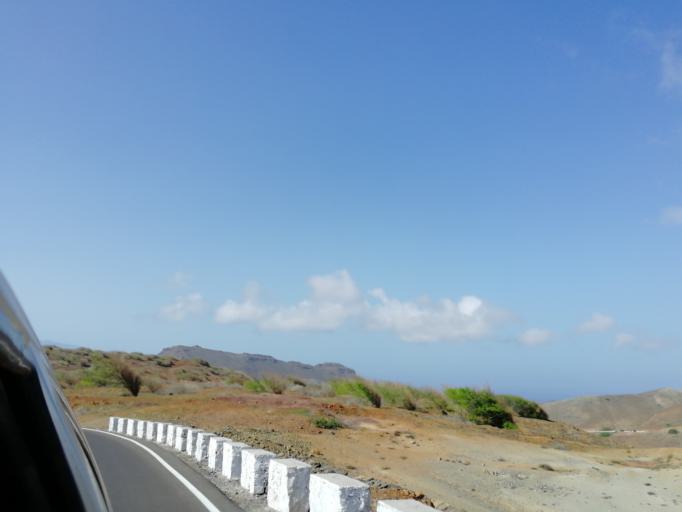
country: CV
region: Sao Vicente
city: Mindelo
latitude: 16.8765
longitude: -24.9457
